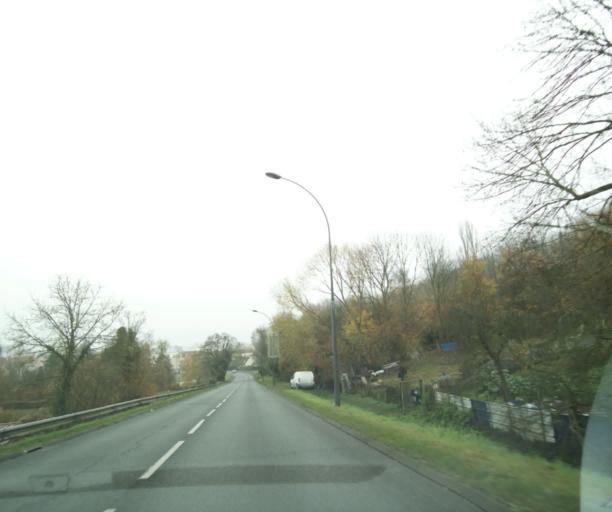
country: FR
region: Ile-de-France
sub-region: Departement de Seine-Saint-Denis
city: Vaujours
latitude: 48.9277
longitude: 2.5698
